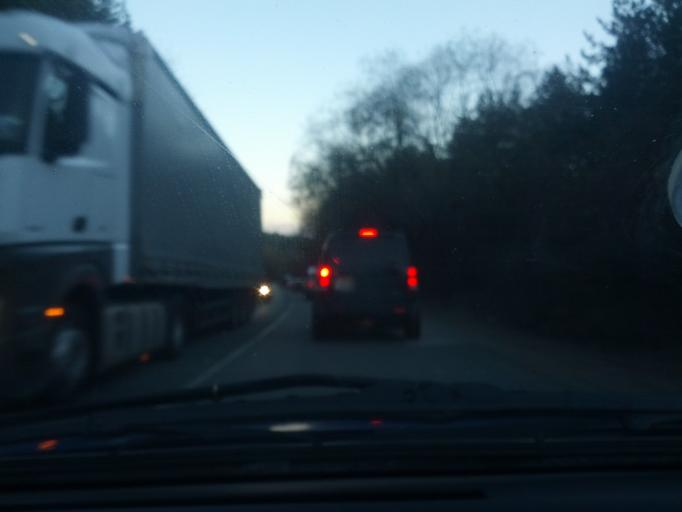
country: BG
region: Vratsa
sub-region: Obshtina Mezdra
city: Mezdra
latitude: 43.0134
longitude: 23.6926
